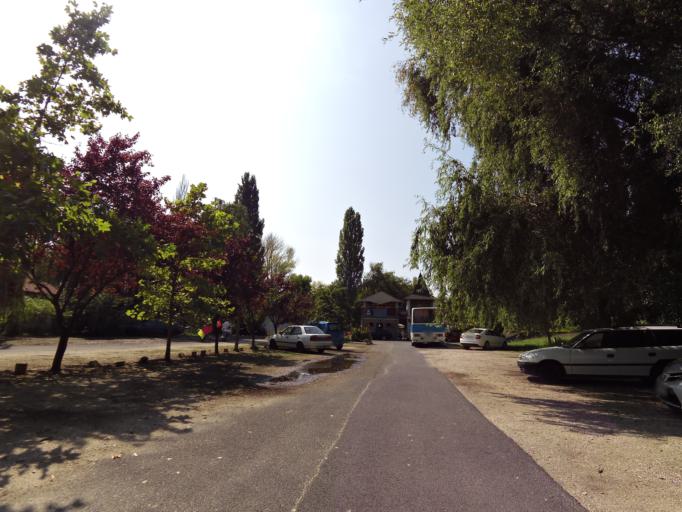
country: HU
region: Zala
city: Vonyarcvashegy
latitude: 46.7888
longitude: 17.3857
